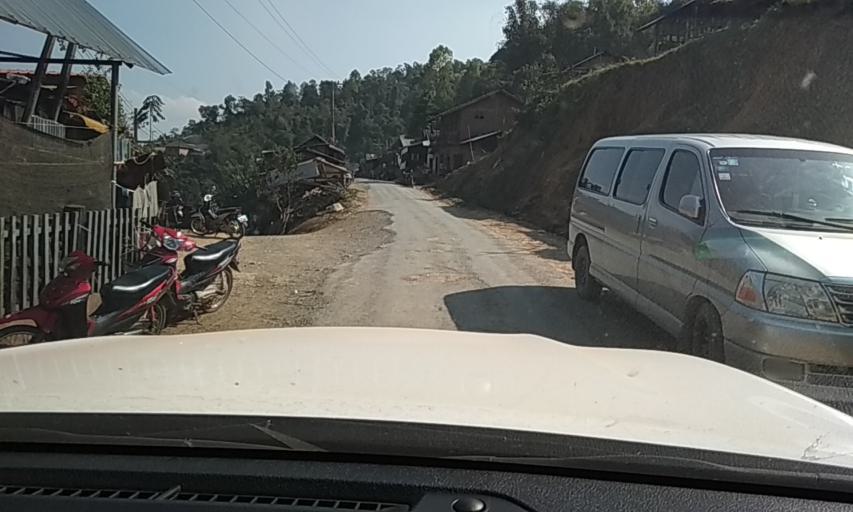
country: LA
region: Phongsali
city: Phongsali
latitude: 21.6634
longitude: 102.0895
